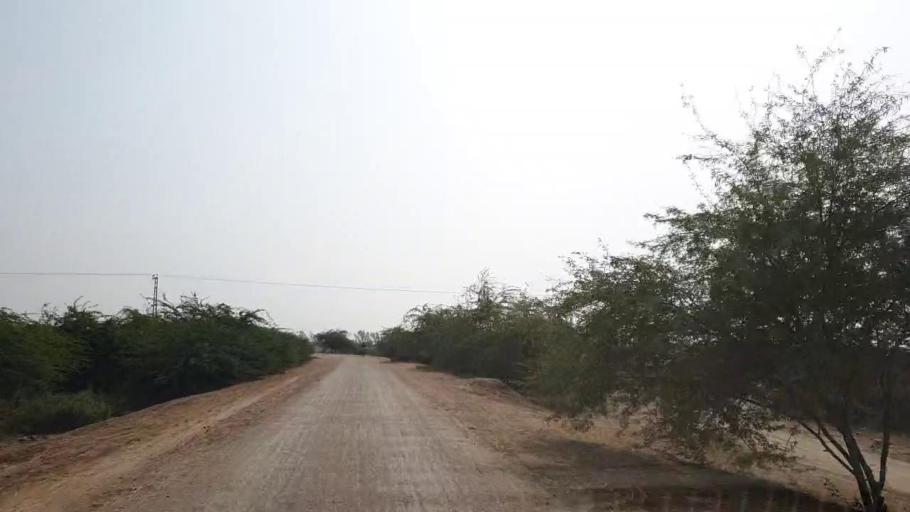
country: PK
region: Sindh
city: Matli
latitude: 24.9993
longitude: 68.5733
